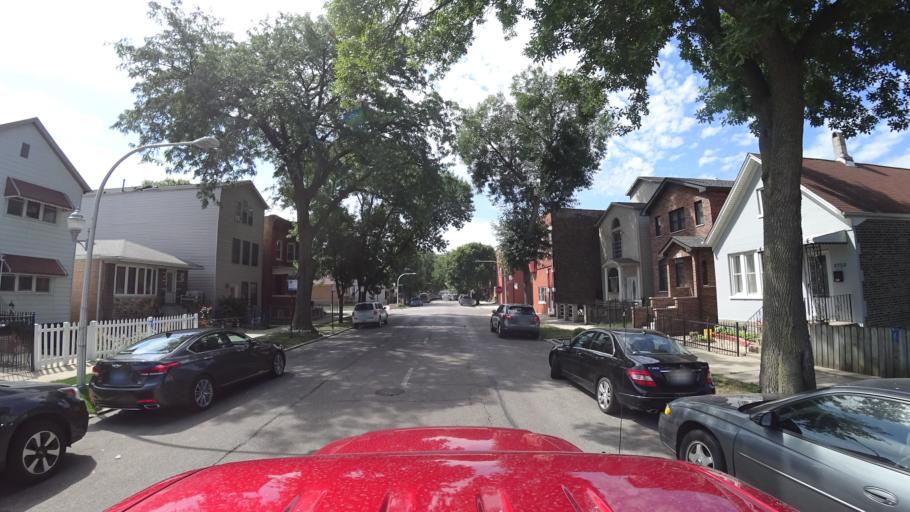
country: US
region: Illinois
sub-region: Cook County
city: Chicago
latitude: 41.8258
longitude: -87.6448
